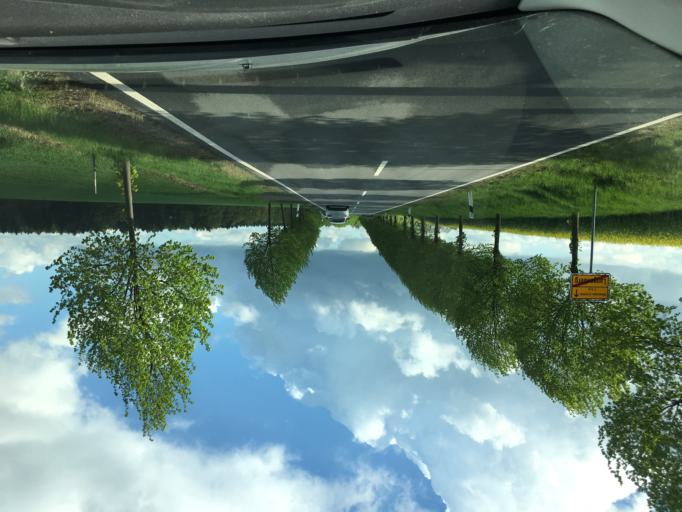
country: DE
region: Saxony
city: Hohenstein-Ernstthal
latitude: 50.8293
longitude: 12.7048
